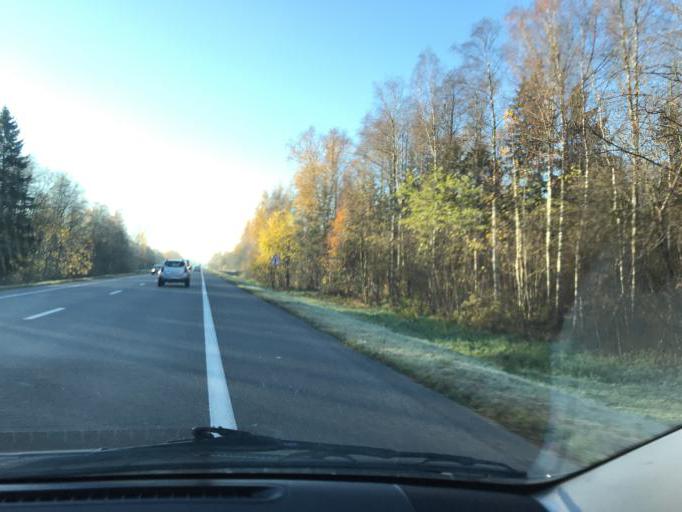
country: BY
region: Vitebsk
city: Vitebsk
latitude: 54.9795
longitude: 30.3469
